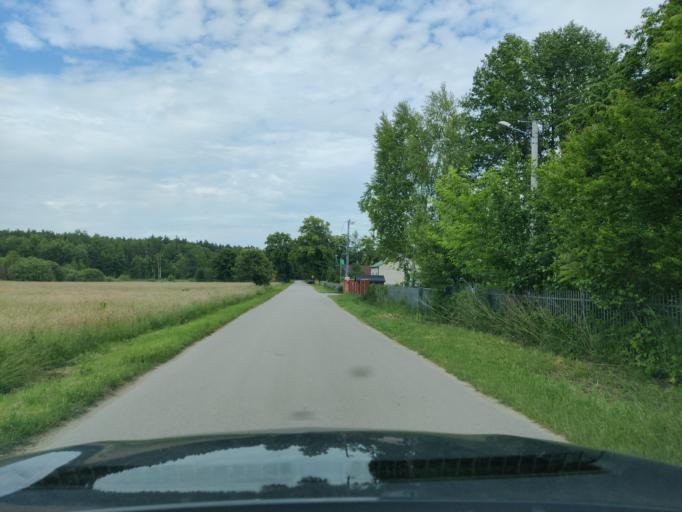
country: PL
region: Masovian Voivodeship
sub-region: Powiat pultuski
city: Obryte
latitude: 52.7364
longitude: 21.1711
